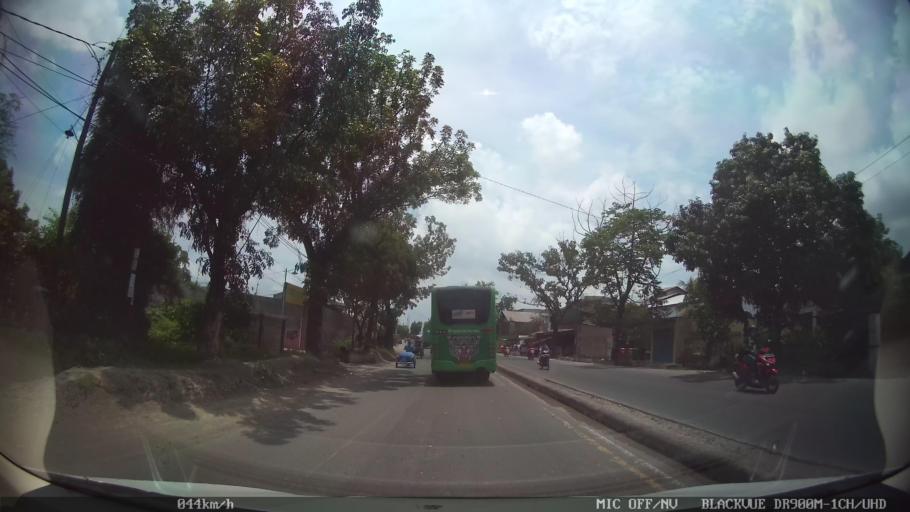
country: ID
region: North Sumatra
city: Labuhan Deli
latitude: 3.7134
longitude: 98.6794
